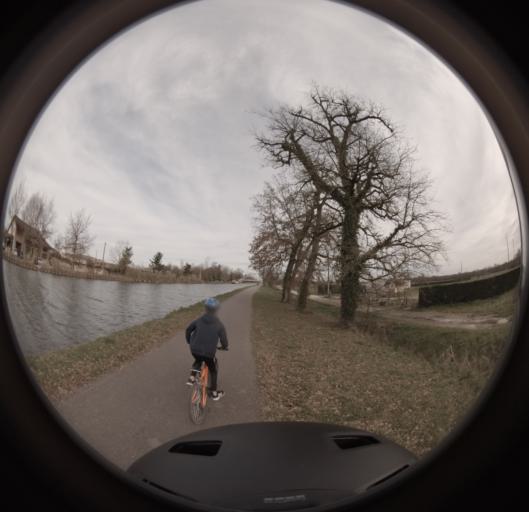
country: FR
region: Midi-Pyrenees
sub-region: Departement du Tarn-et-Garonne
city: Montech
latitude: 43.9838
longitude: 1.2611
